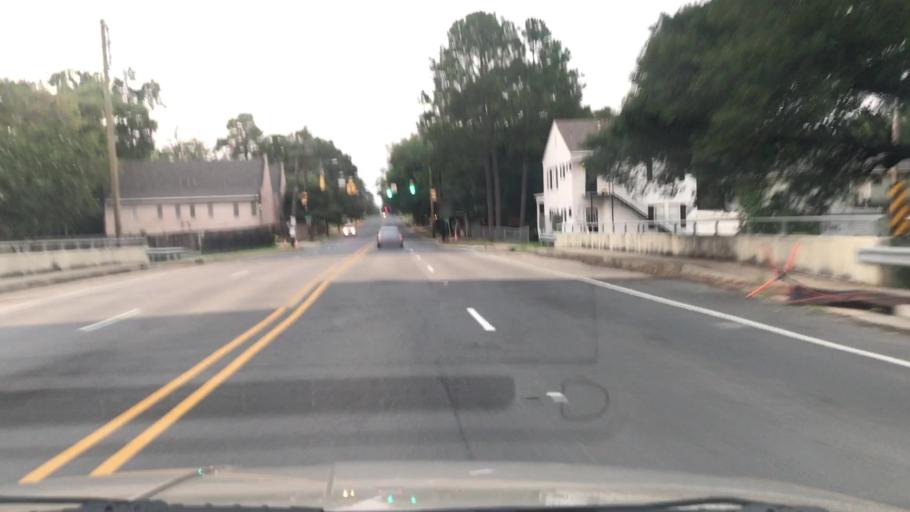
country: US
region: Louisiana
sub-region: Bossier Parish
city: Bossier City
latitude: 32.4682
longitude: -93.7460
